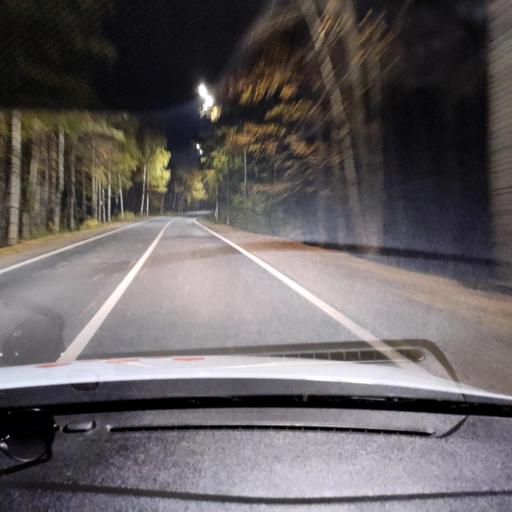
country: RU
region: Tatarstan
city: Verkhniy Uslon
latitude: 55.6333
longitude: 49.0184
